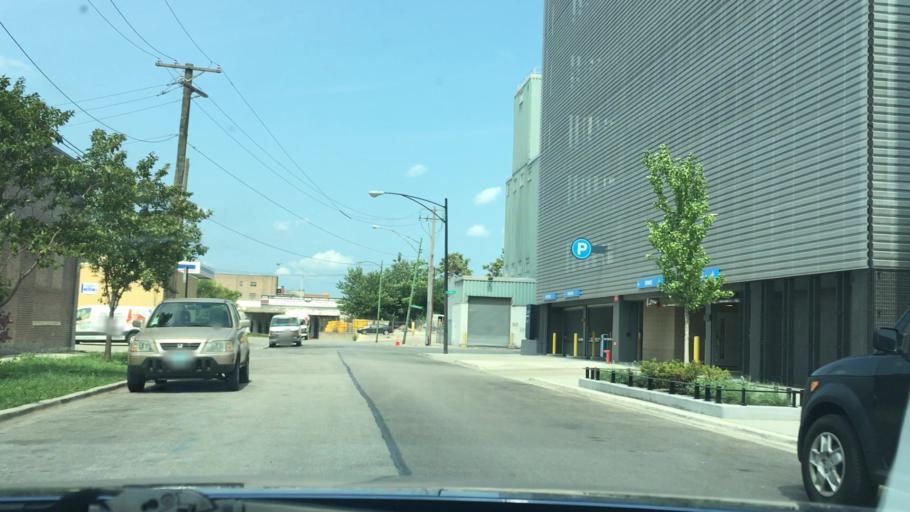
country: US
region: Illinois
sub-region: Cook County
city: Chicago
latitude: 41.8871
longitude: -87.6608
